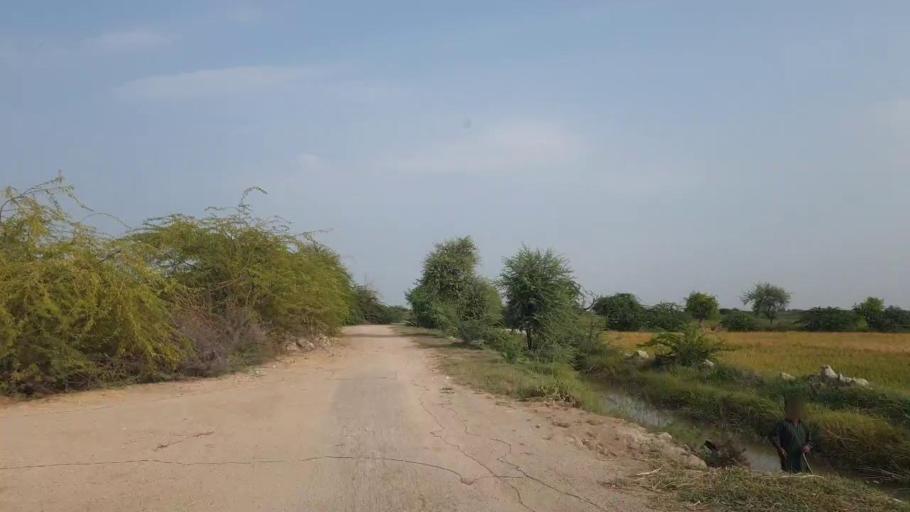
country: PK
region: Sindh
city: Kadhan
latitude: 24.4590
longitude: 68.8002
